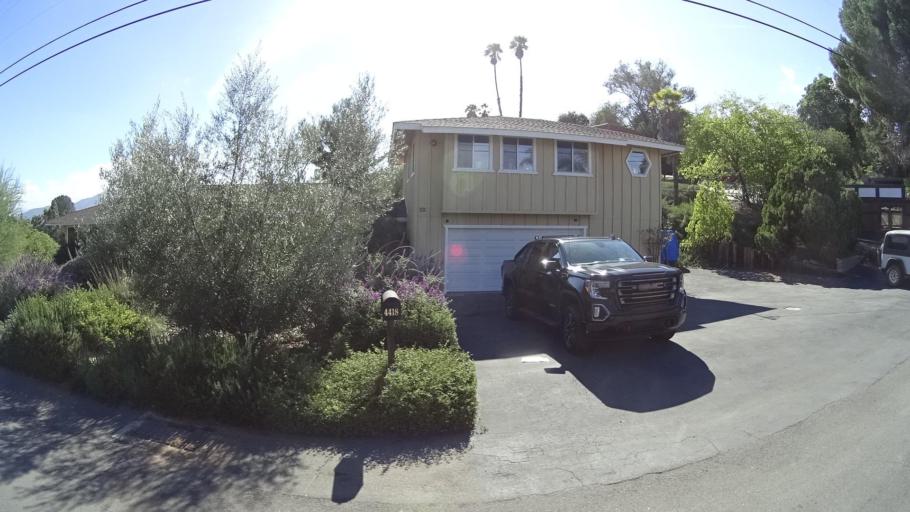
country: US
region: California
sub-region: San Diego County
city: Casa de Oro-Mount Helix
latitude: 32.7600
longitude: -116.9560
